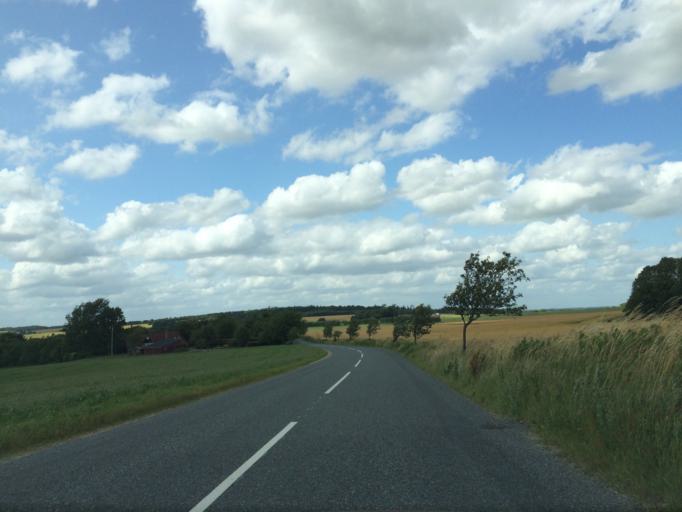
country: DK
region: Central Jutland
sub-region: Skanderborg Kommune
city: Ry
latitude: 56.1820
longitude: 9.7727
